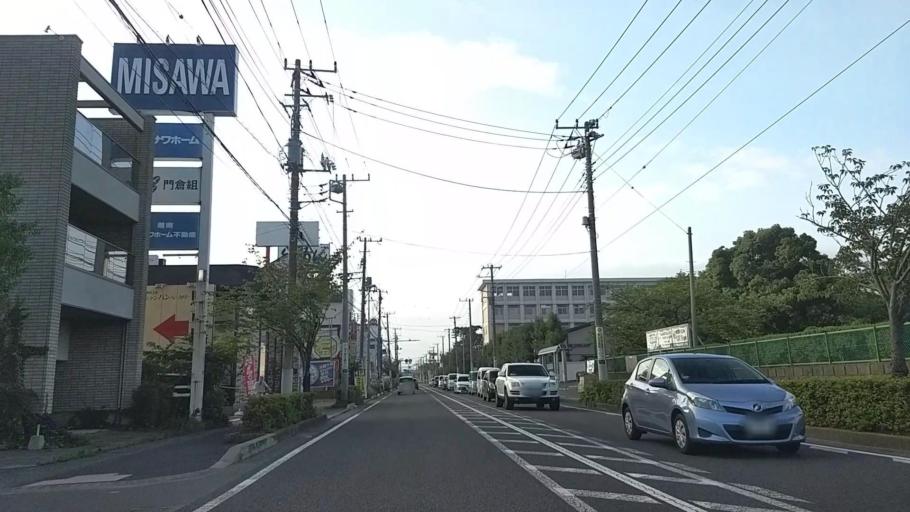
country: JP
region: Kanagawa
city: Hiratsuka
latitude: 35.3301
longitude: 139.3276
